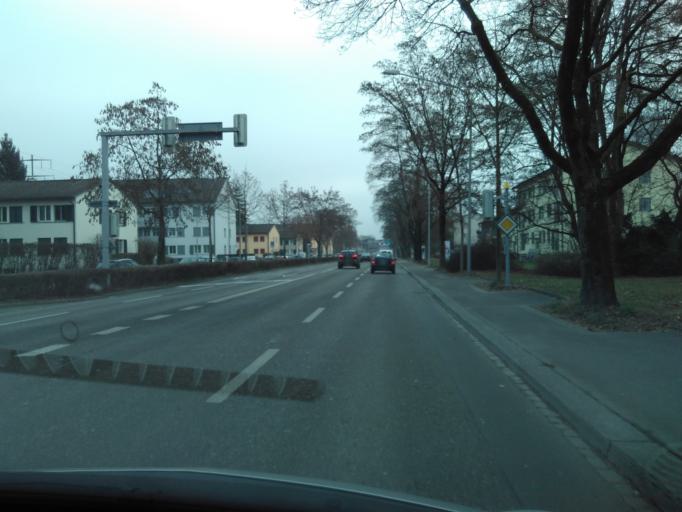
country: CH
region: Zurich
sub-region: Bezirk Zuerich
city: Zuerich (Kreis 12) / Schwamendingen-Mitte
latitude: 47.4097
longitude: 8.5758
